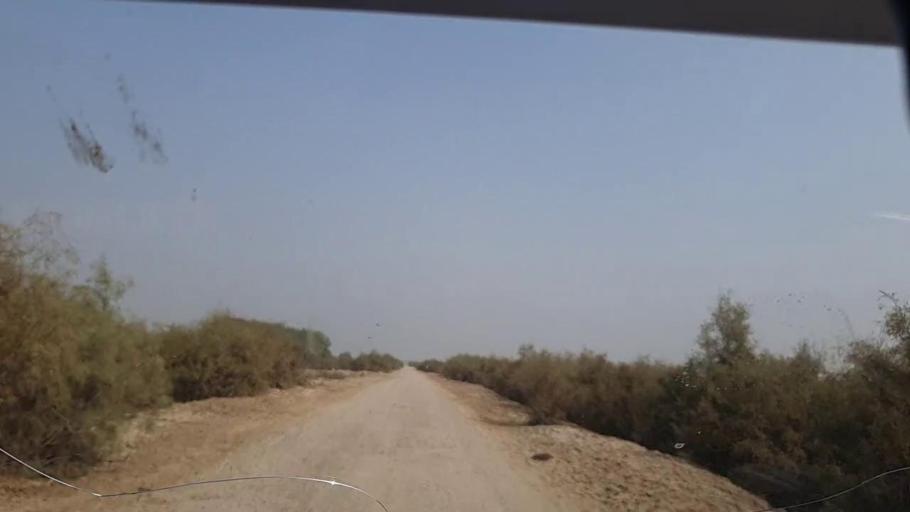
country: PK
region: Sindh
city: Shikarpur
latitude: 28.0380
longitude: 68.6412
